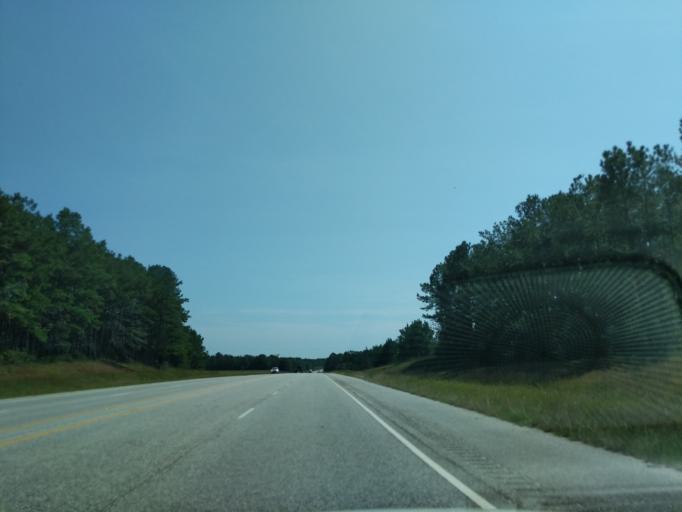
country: US
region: Alabama
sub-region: Butler County
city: Georgiana
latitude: 31.5027
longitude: -86.6989
